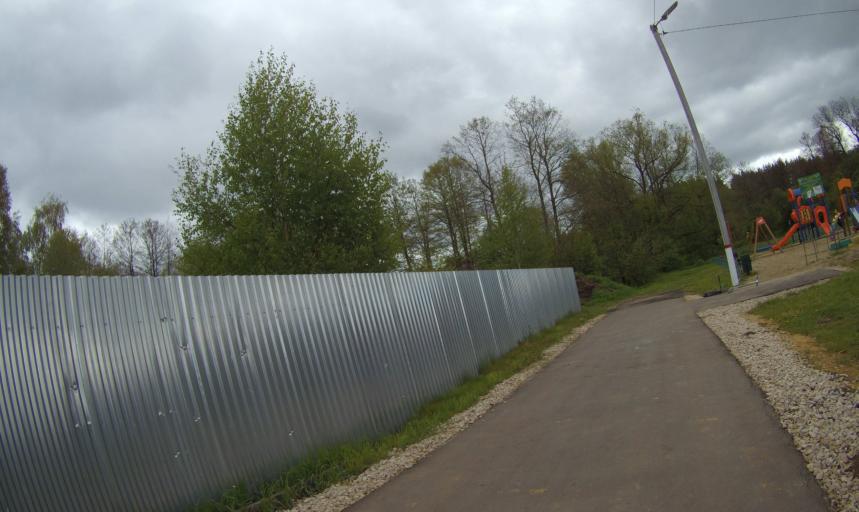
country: RU
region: Moskovskaya
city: Rechitsy
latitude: 55.5396
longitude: 38.4304
